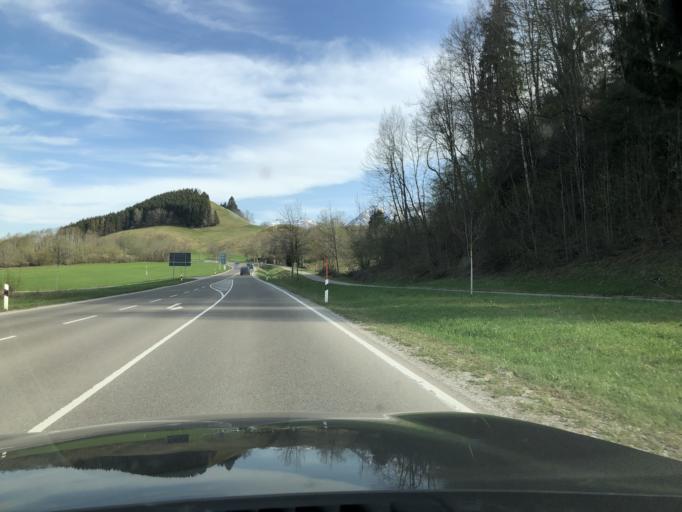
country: DE
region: Bavaria
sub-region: Swabia
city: Pfronten
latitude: 47.6028
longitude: 10.5407
